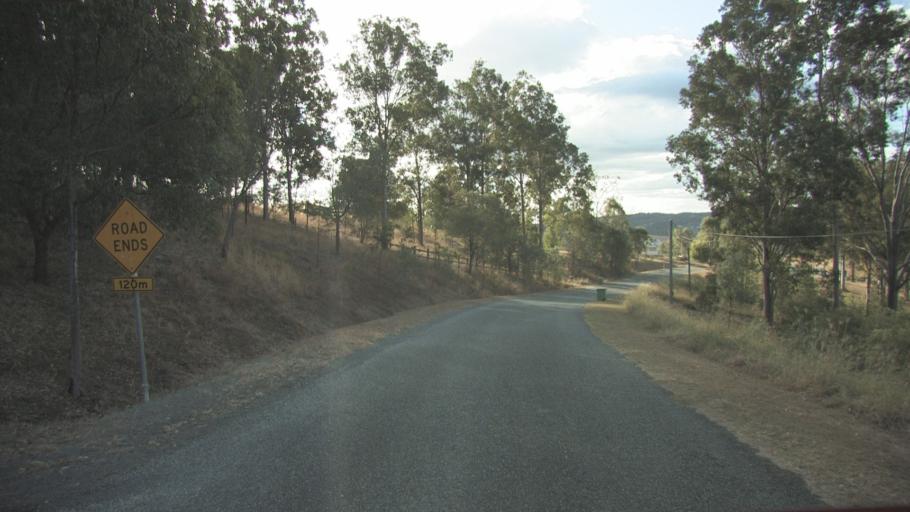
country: AU
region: Queensland
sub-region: Logan
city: Cedar Vale
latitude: -27.8988
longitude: 153.0717
